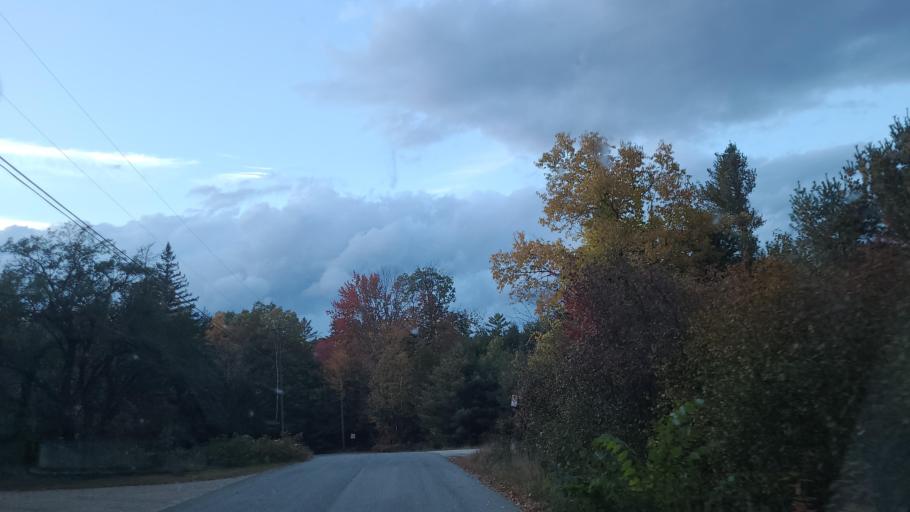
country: US
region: New Hampshire
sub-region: Carroll County
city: North Conway
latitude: 44.1517
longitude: -71.1775
